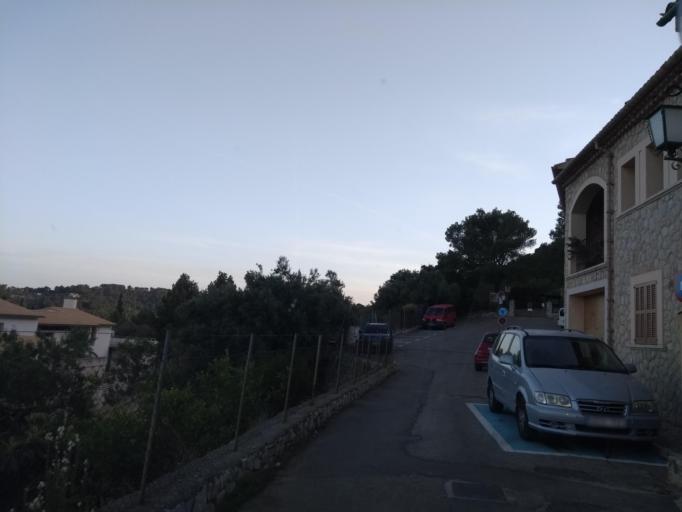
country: ES
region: Balearic Islands
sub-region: Illes Balears
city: Selva
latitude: 39.7700
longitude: 2.8993
